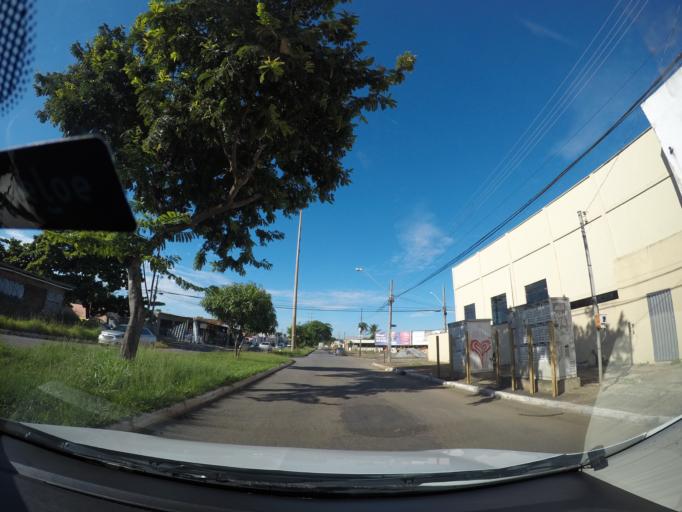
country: BR
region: Goias
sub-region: Goiania
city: Goiania
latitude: -16.7292
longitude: -49.3073
